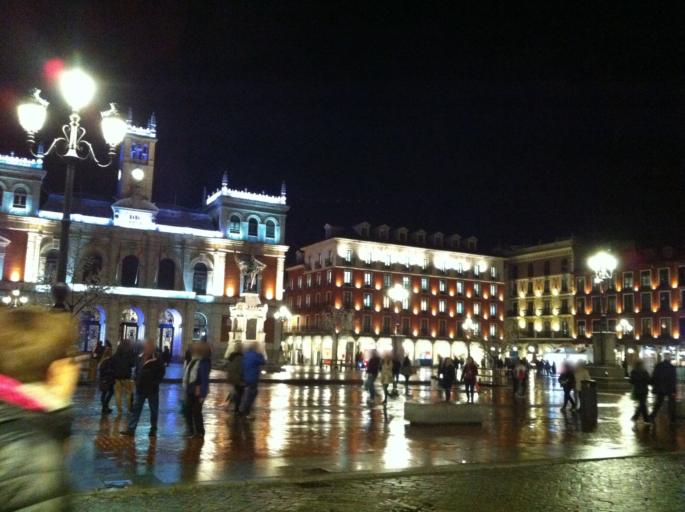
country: ES
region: Castille and Leon
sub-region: Provincia de Valladolid
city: Valladolid
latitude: 41.6519
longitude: -4.7286
